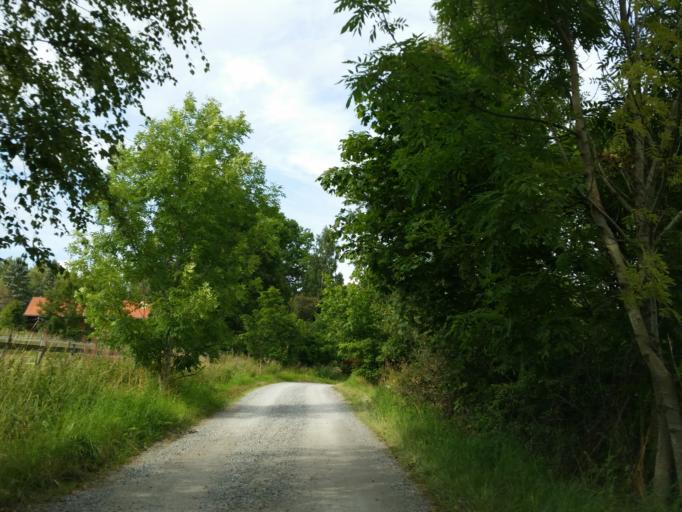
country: SE
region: Soedermanland
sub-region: Strangnas Kommun
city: Mariefred
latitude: 59.2204
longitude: 17.2331
